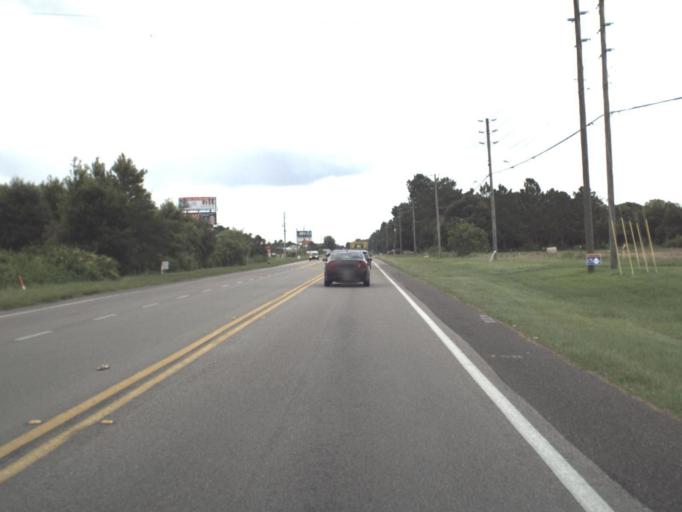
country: US
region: Florida
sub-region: Pasco County
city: Wesley Chapel
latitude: 28.2313
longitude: -82.2958
